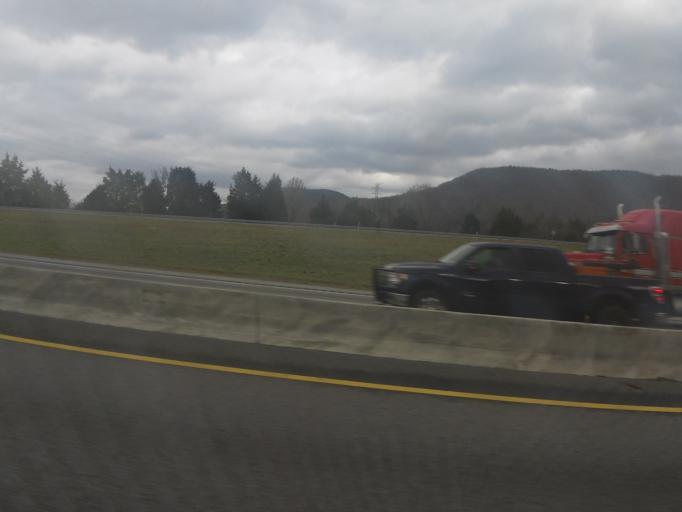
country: US
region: Tennessee
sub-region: Marion County
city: Jasper
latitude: 35.0157
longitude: -85.5414
